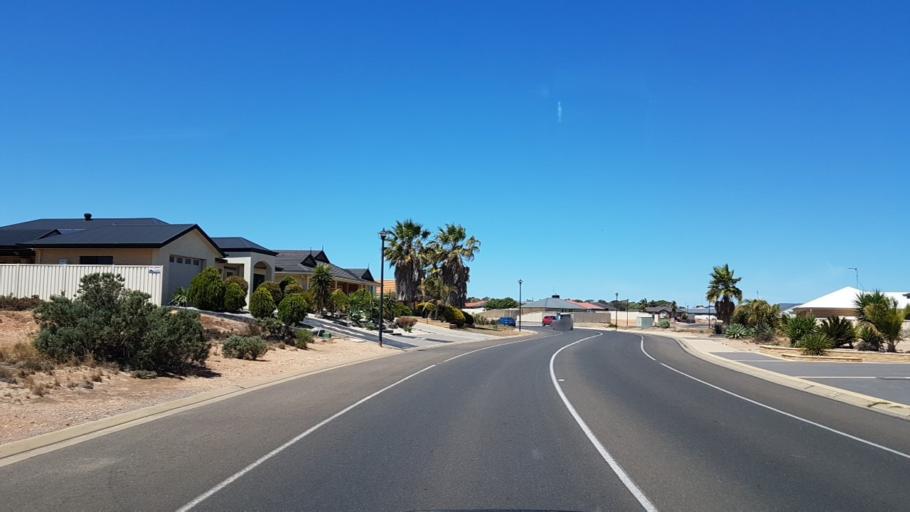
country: AU
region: South Australia
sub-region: Copper Coast
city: Wallaroo
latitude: -33.9197
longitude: 137.6423
